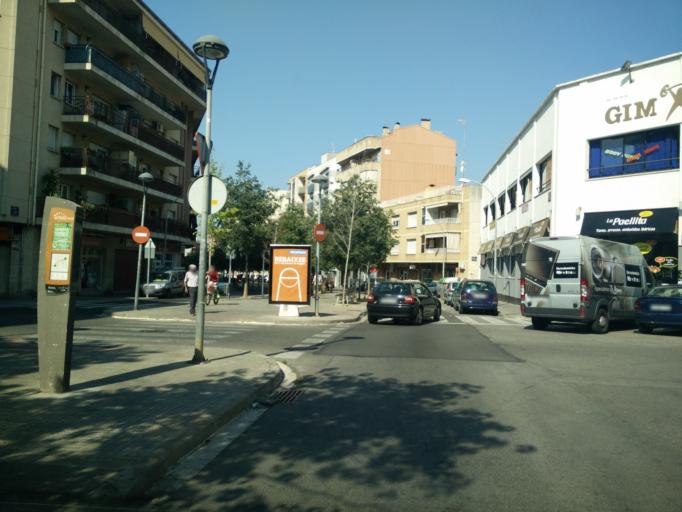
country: ES
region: Catalonia
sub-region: Provincia de Barcelona
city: Terrassa
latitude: 41.5765
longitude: 2.0197
